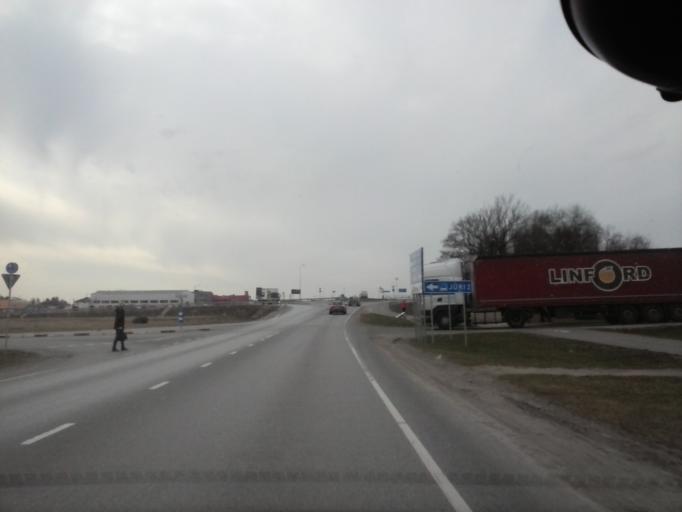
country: EE
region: Harju
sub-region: Rae vald
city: Jueri
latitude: 59.3569
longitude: 24.8941
